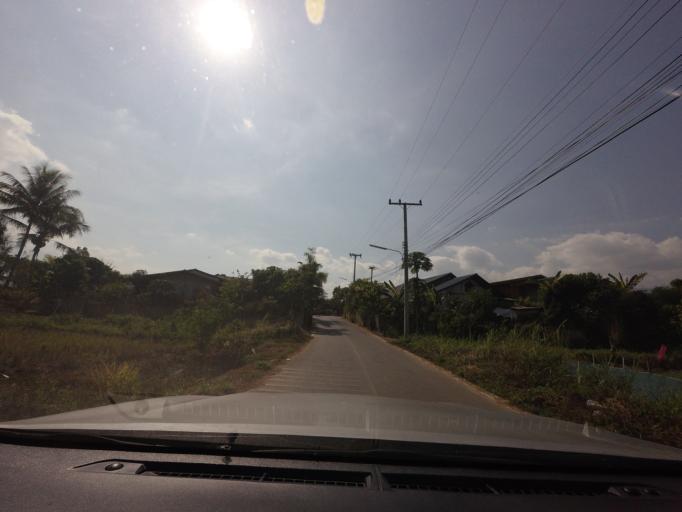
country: TH
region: Mae Hong Son
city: Wiang Nuea
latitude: 19.3862
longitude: 98.4405
